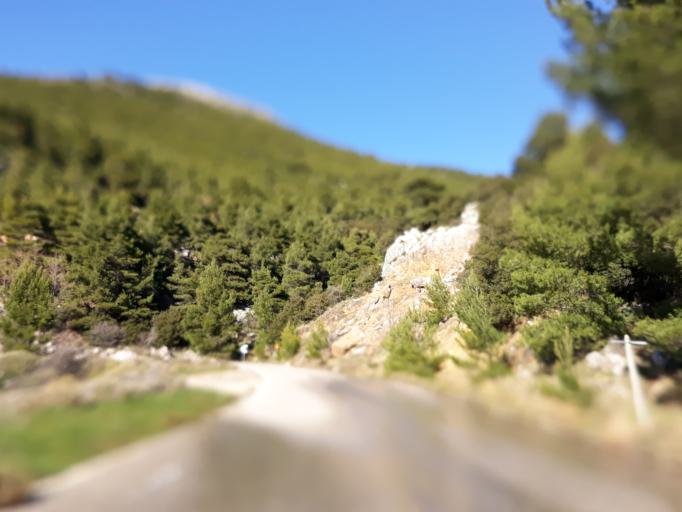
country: GR
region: Attica
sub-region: Nomarchia Dytikis Attikis
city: Fyli
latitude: 38.1446
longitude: 23.6451
